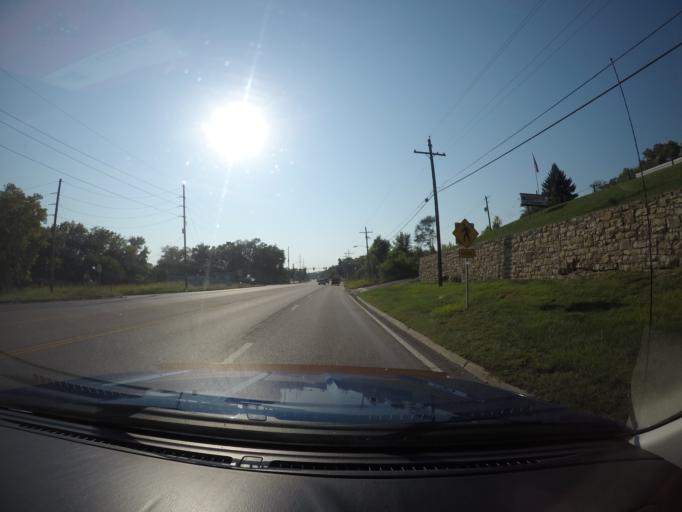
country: US
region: Kansas
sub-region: Wyandotte County
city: Edwardsville
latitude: 39.0621
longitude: -94.8198
